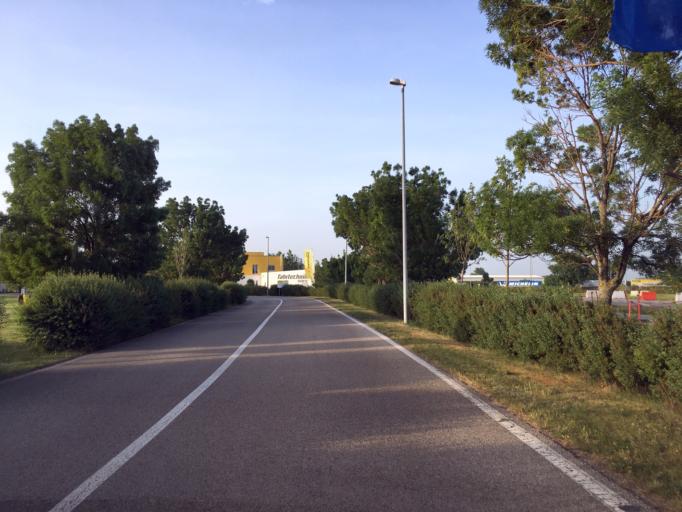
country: AT
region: Lower Austria
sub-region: Politischer Bezirk Baden
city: Teesdorf
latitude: 47.9597
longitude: 16.2724
